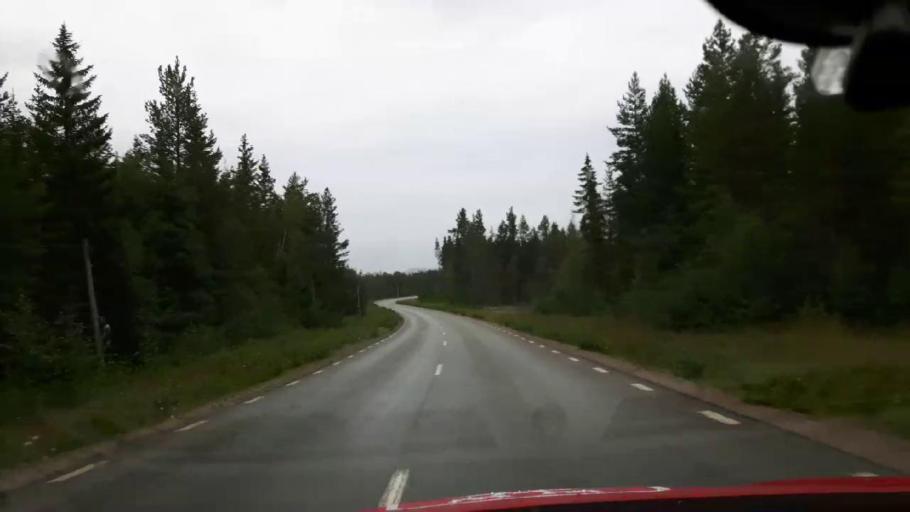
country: SE
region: Jaemtland
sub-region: OEstersunds Kommun
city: Brunflo
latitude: 62.8226
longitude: 14.9996
